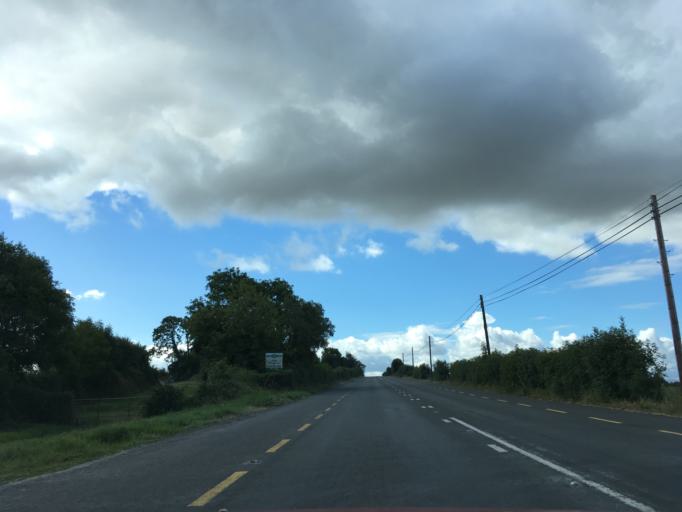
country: IE
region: Munster
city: Cahir
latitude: 52.4223
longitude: -7.8884
